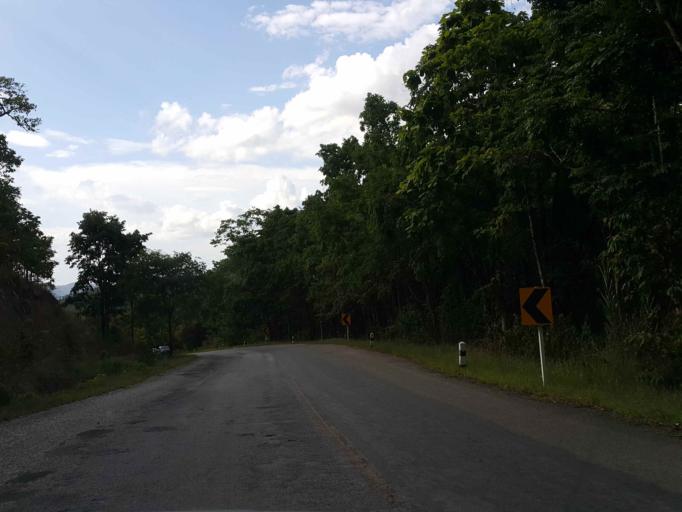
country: TH
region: Lampang
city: Thoen
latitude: 17.6280
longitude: 99.3121
